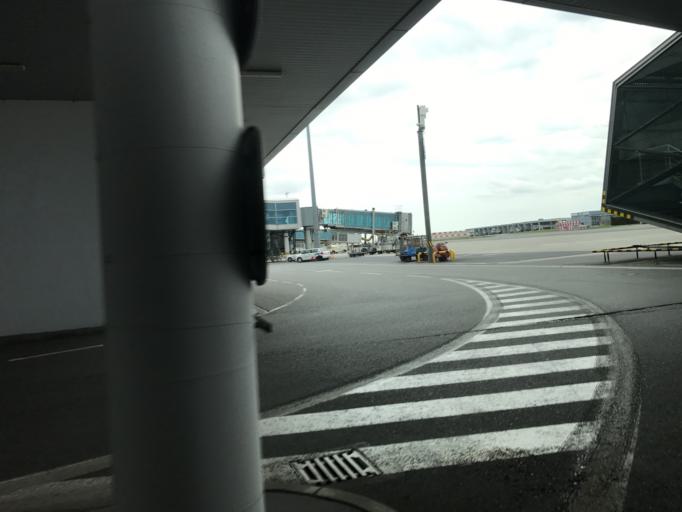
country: CZ
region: Central Bohemia
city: Hostivice
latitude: 50.1068
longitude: 14.2624
